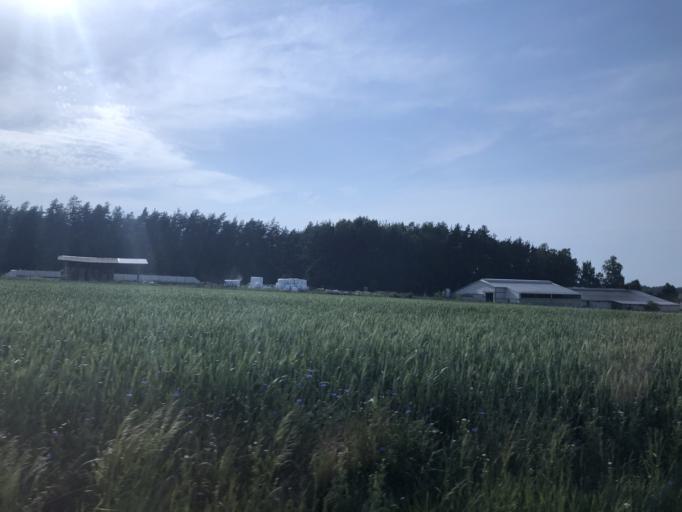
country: PL
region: Podlasie
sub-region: Lomza
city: Lomza
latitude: 53.1417
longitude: 22.0063
